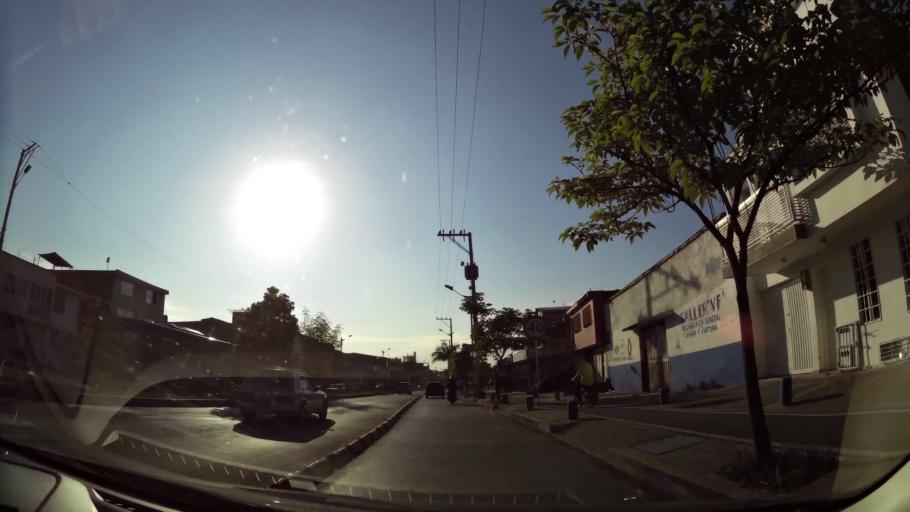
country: CO
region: Valle del Cauca
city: Cali
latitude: 3.4344
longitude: -76.5139
